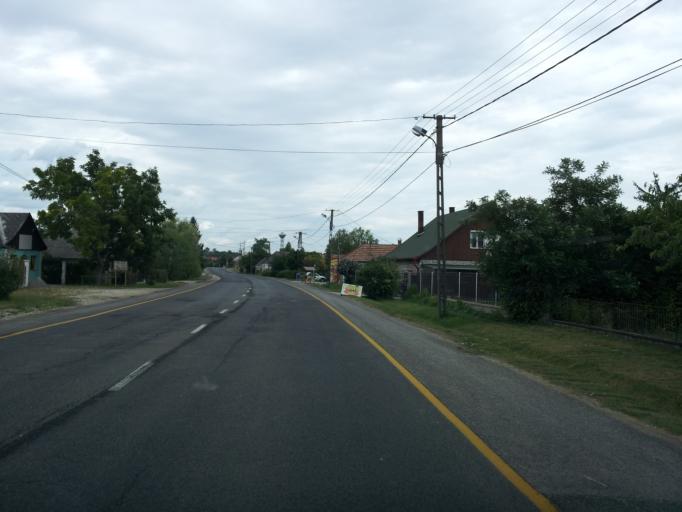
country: HU
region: Fejer
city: Lepseny
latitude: 46.9978
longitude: 18.2491
